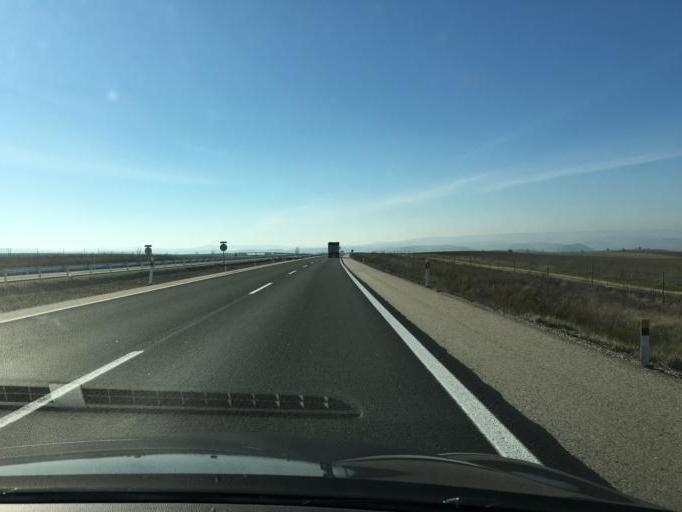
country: ES
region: Castille and Leon
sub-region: Provincia de Burgos
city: Grisalena
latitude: 42.5598
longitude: -3.2731
